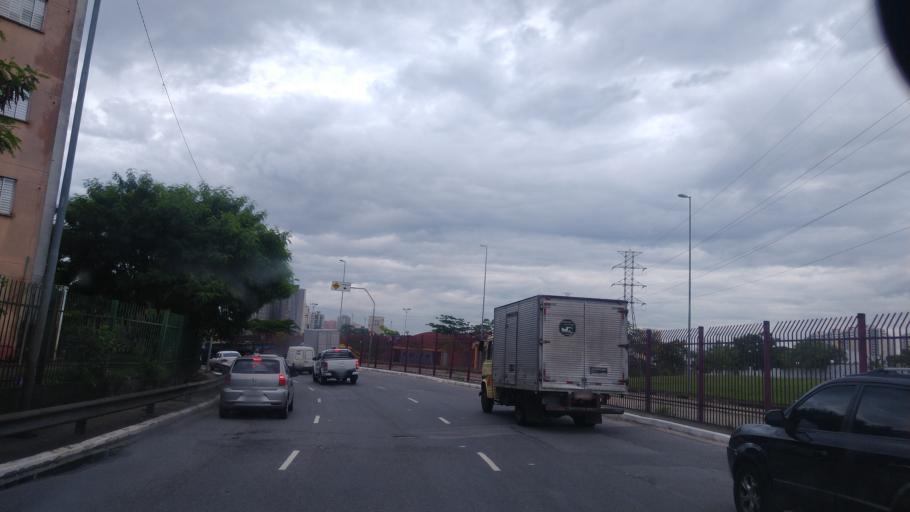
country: BR
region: Sao Paulo
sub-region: Guarulhos
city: Guarulhos
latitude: -23.5185
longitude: -46.5594
